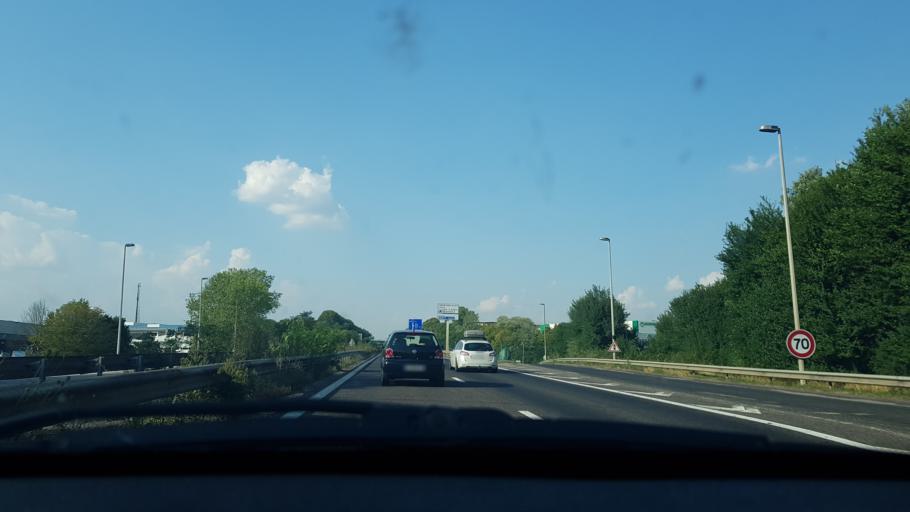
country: FR
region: Lorraine
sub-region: Departement de Meurthe-et-Moselle
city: Ludres
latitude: 48.6153
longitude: 6.1789
